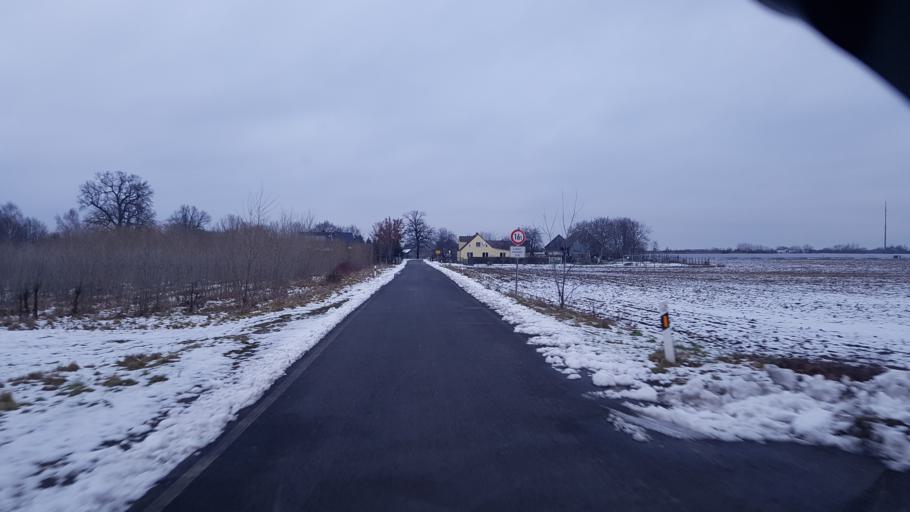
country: DE
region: Brandenburg
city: Vetschau
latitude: 51.7950
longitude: 14.0427
